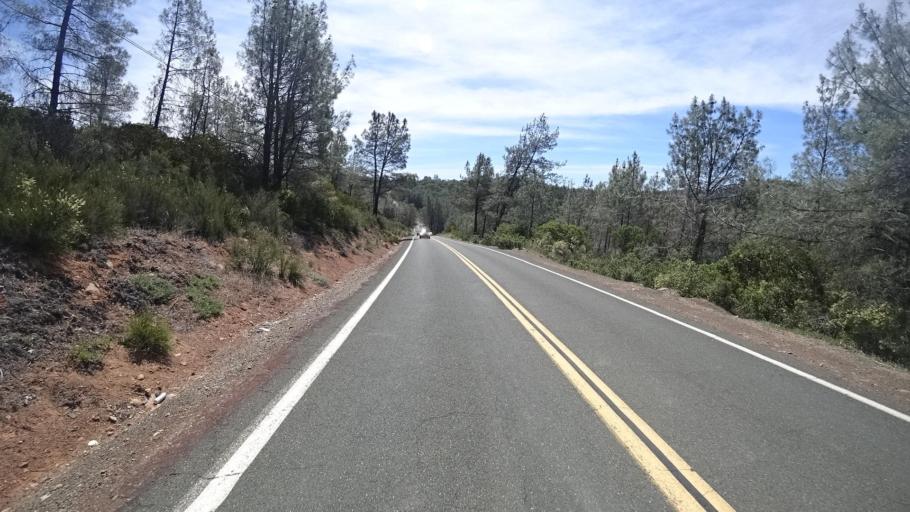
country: US
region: California
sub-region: Lake County
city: Clearlake
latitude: 38.9340
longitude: -122.6617
